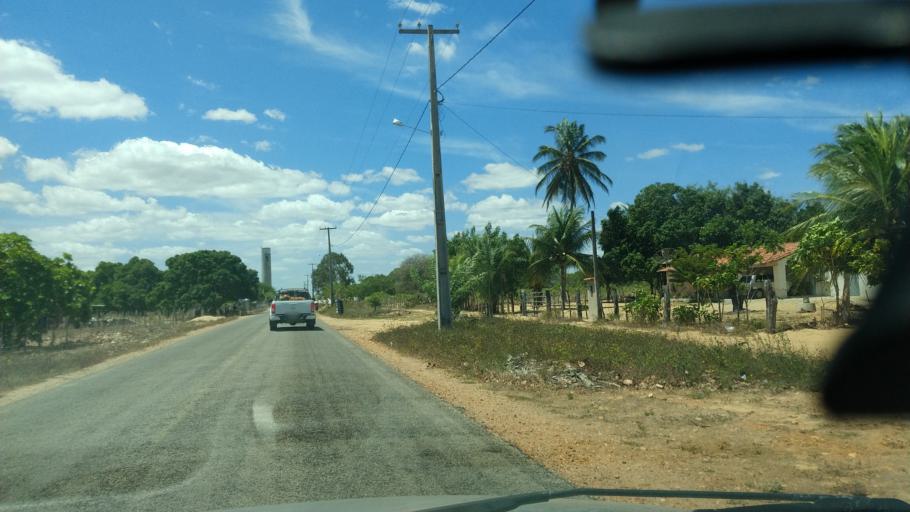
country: BR
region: Rio Grande do Norte
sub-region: Sao Paulo Do Potengi
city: Sao Paulo do Potengi
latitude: -5.9160
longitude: -35.7261
